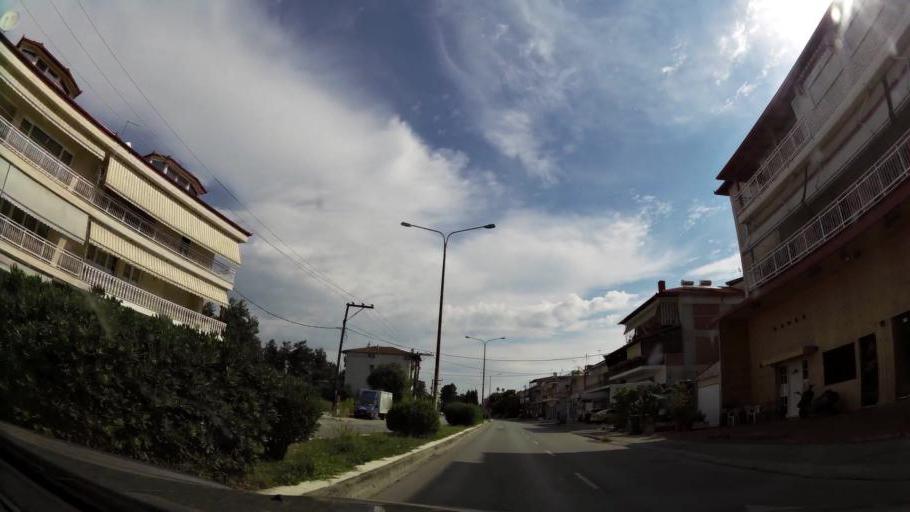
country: GR
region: Central Macedonia
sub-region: Nomos Pierias
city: Katerini
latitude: 40.2782
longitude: 22.5159
